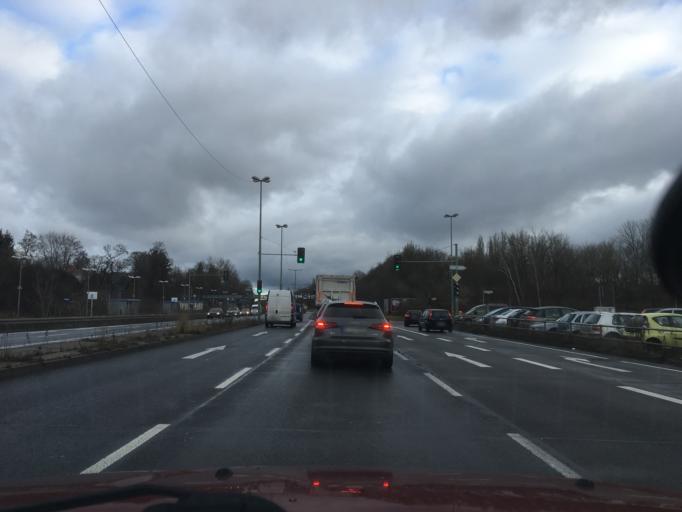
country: DE
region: Berlin
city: Bohnsdorf
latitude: 52.4061
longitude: 13.5575
